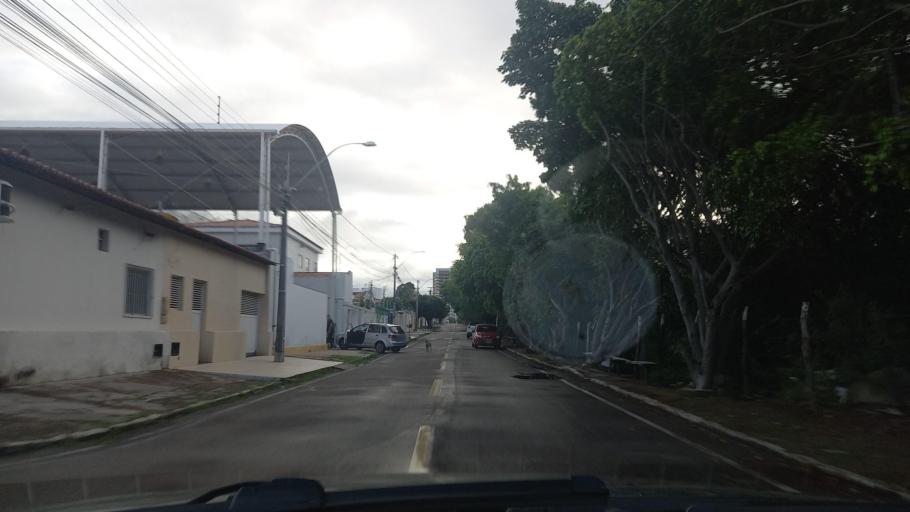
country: BR
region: Bahia
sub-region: Paulo Afonso
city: Paulo Afonso
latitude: -9.3976
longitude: -38.2265
